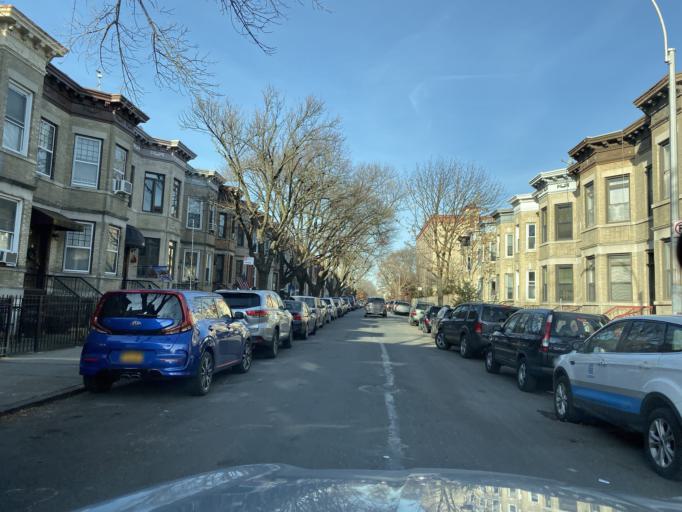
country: US
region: New York
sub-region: Kings County
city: Brooklyn
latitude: 40.6600
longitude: -73.9812
